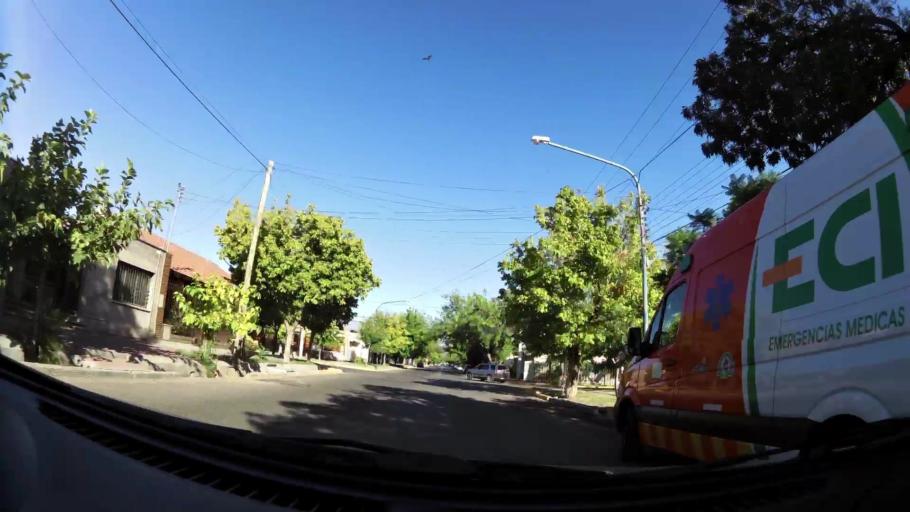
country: AR
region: Mendoza
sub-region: Departamento de Godoy Cruz
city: Godoy Cruz
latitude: -32.9310
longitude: -68.8335
